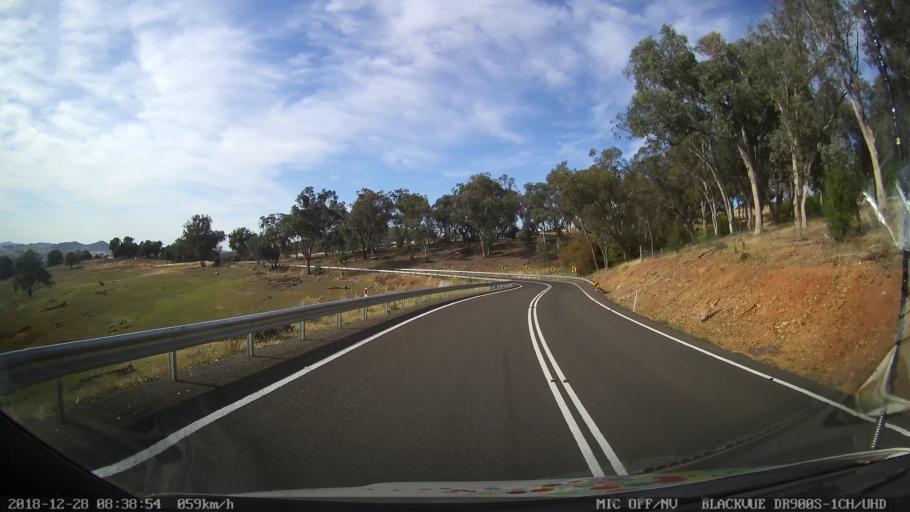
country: AU
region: New South Wales
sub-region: Upper Lachlan Shire
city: Crookwell
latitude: -34.0079
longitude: 149.3166
